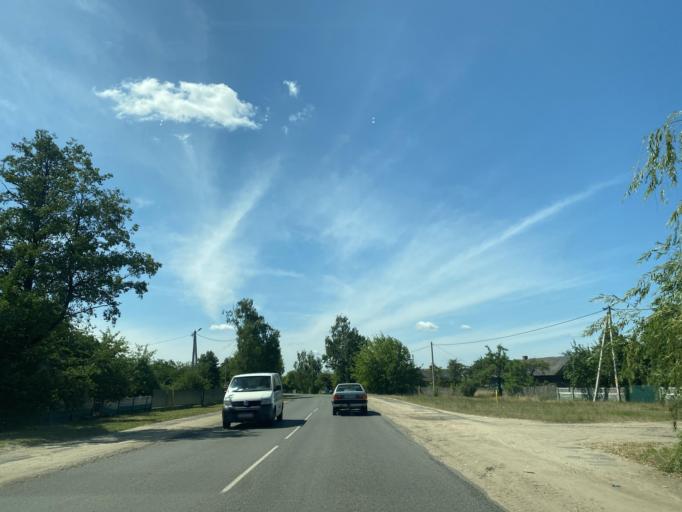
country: BY
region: Brest
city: Ivanava
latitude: 52.1650
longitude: 25.5482
